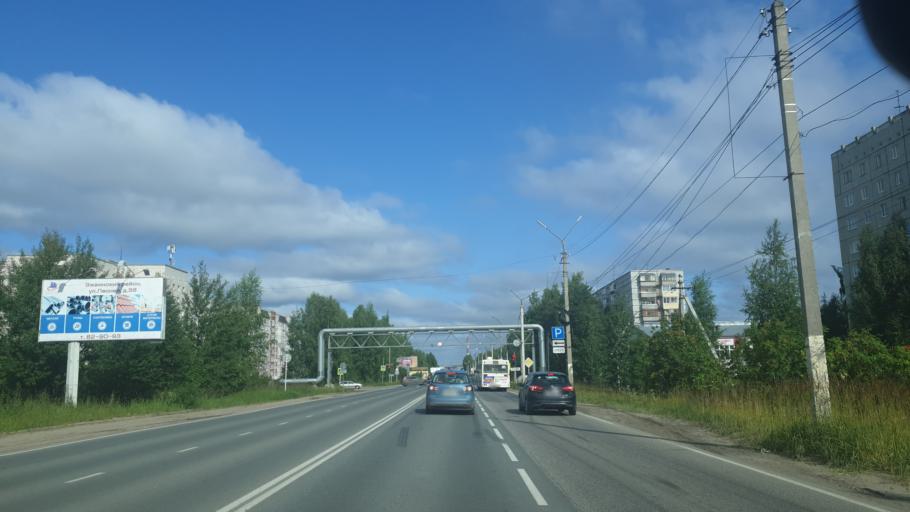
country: RU
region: Komi Republic
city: Ezhva
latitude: 61.7859
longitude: 50.7449
